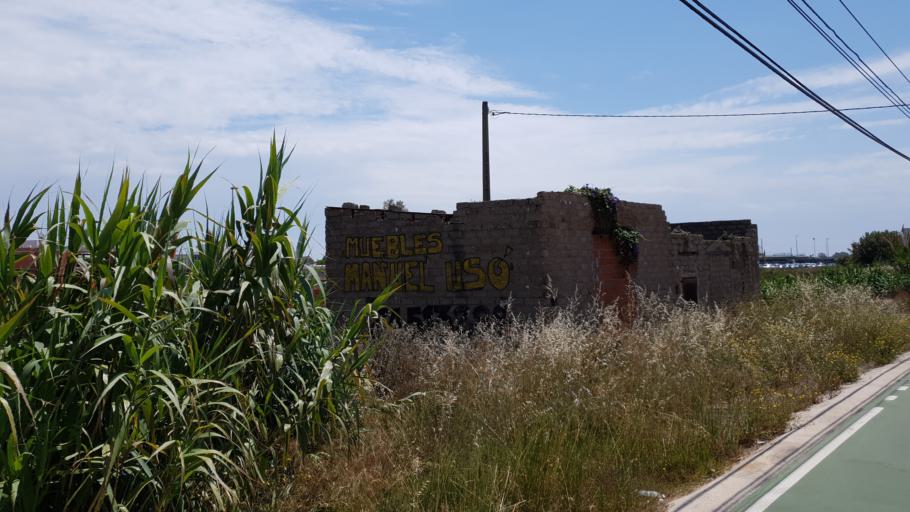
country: ES
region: Valencia
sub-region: Provincia de Castello
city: Burriana
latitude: 39.8810
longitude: -0.0796
